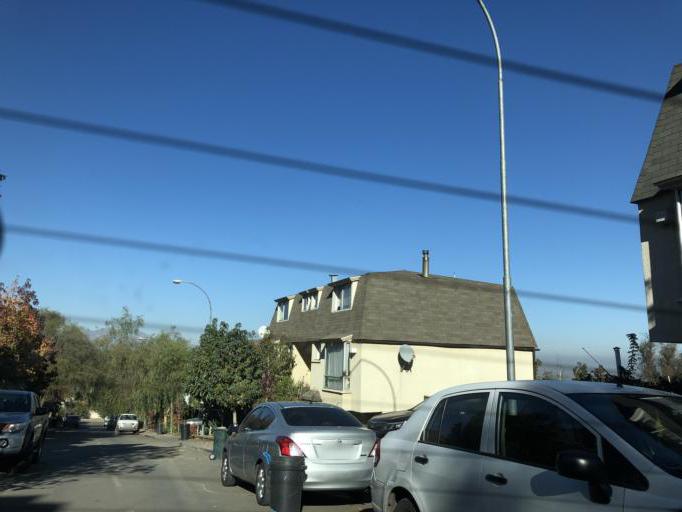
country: CL
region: Santiago Metropolitan
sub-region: Provincia de Cordillera
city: Puente Alto
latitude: -33.5541
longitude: -70.5339
